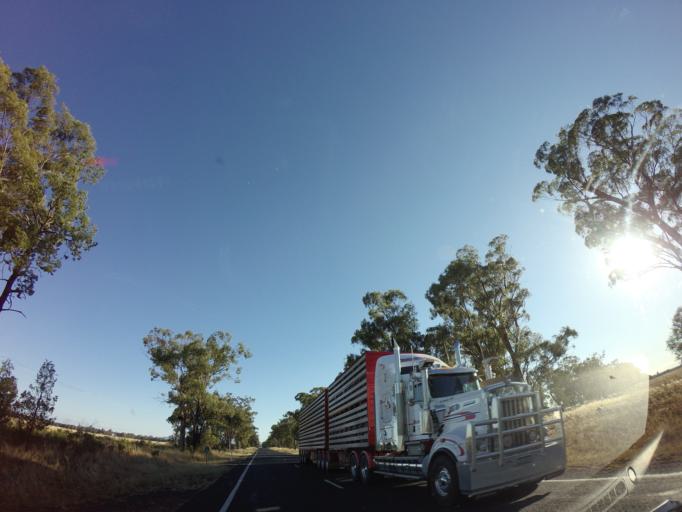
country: AU
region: New South Wales
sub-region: Gilgandra
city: Gilgandra
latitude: -31.5829
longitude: 148.7763
